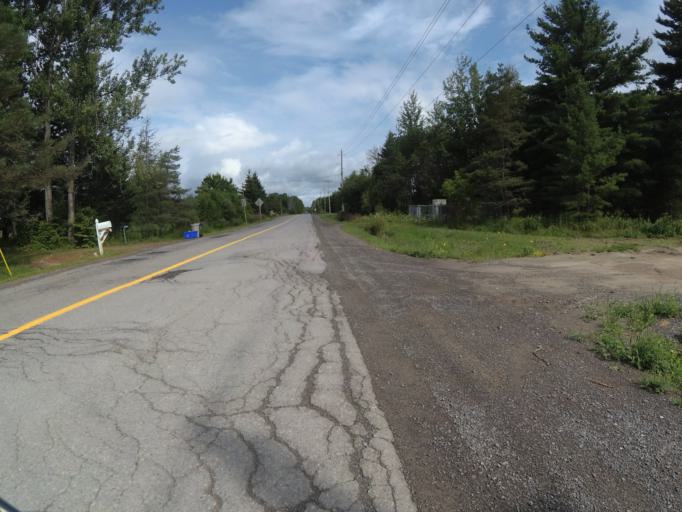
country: CA
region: Ontario
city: Clarence-Rockland
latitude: 45.4925
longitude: -75.3157
